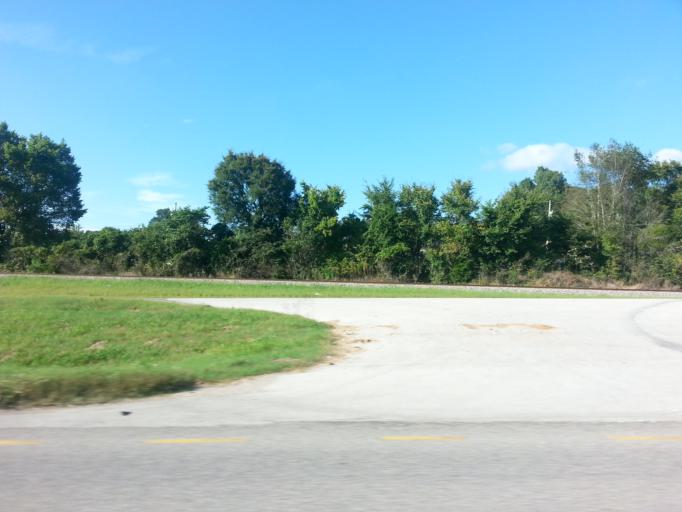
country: US
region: Alabama
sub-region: Colbert County
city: Tuscumbia
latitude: 34.7103
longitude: -87.7701
